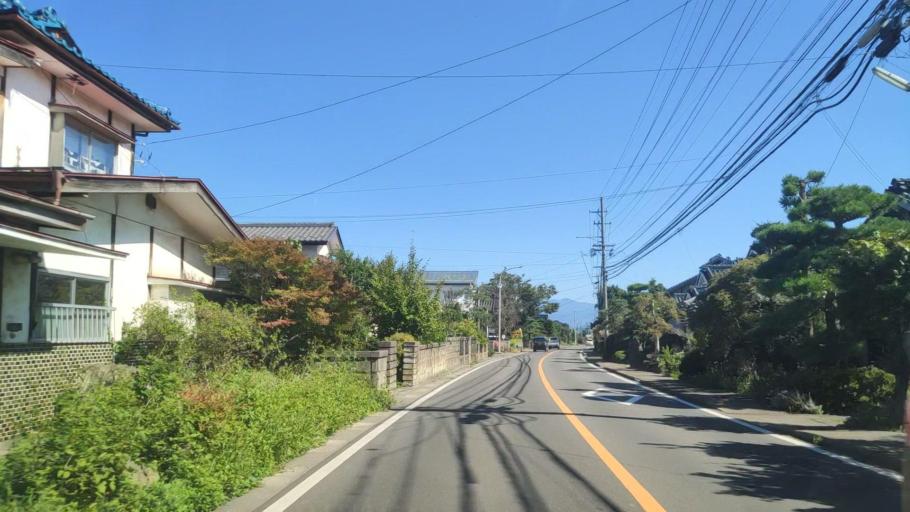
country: JP
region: Nagano
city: Shiojiri
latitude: 36.1386
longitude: 137.9388
